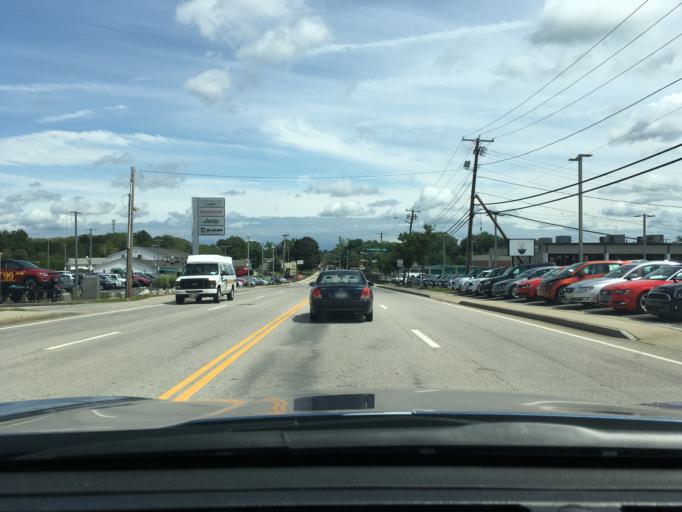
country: US
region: Rhode Island
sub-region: Providence County
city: Johnston
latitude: 41.8270
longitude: -71.5113
